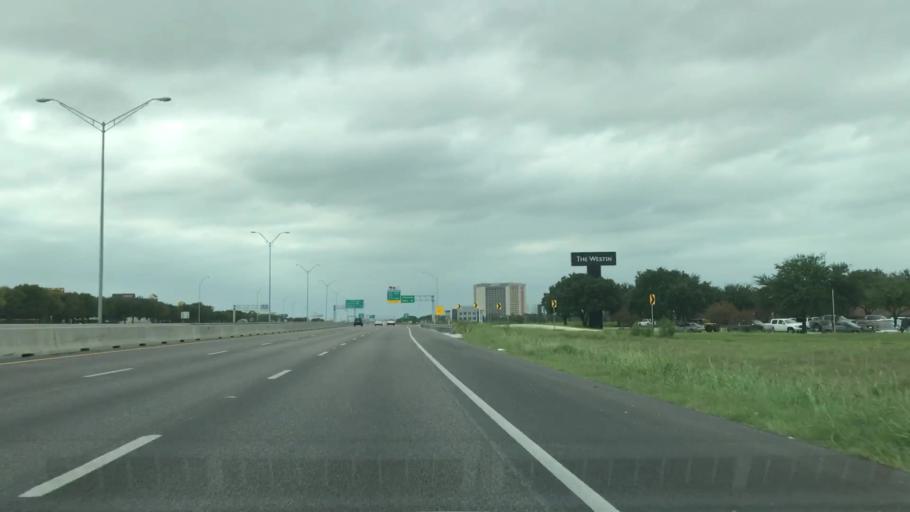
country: US
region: Texas
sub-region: Dallas County
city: Coppell
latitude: 32.9157
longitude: -97.0086
